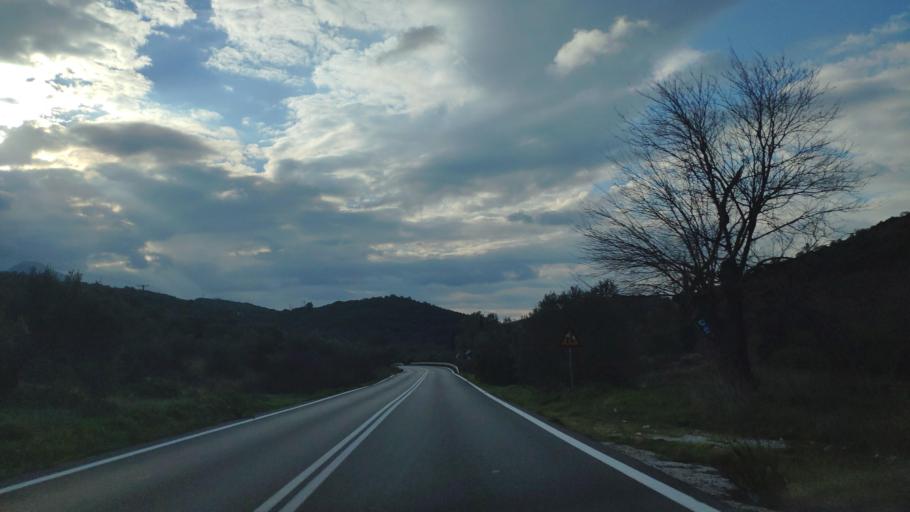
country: GR
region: Peloponnese
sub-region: Nomos Korinthias
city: Ayios Vasilios
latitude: 37.7763
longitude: 22.7248
